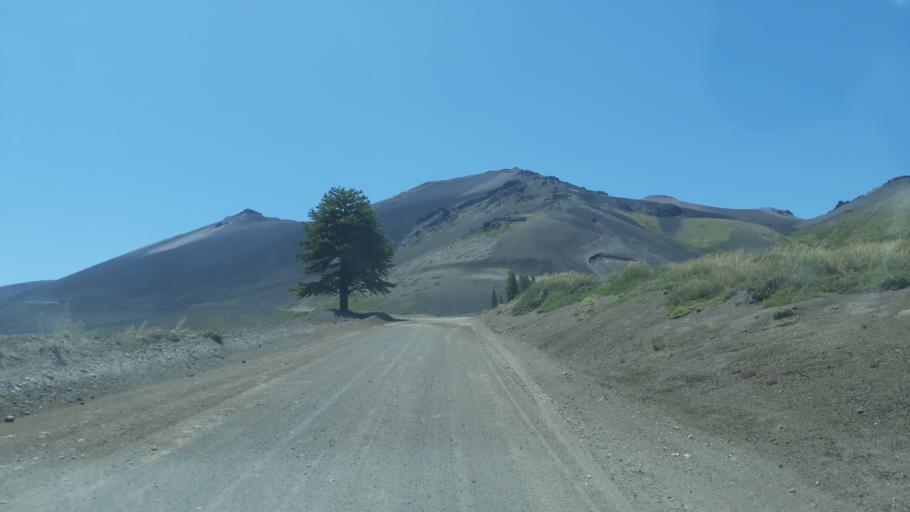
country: CL
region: Araucania
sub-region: Provincia de Cautin
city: Vilcun
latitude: -38.4171
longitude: -71.5437
